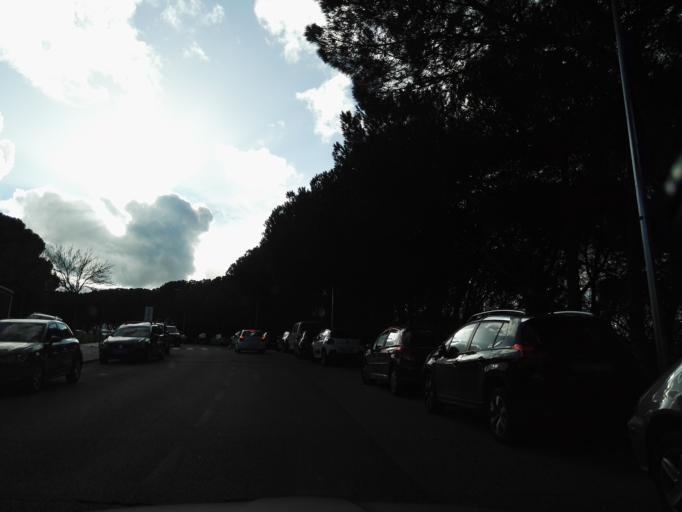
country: PT
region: Lisbon
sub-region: Loures
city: Moscavide
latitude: 38.7679
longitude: -9.1162
